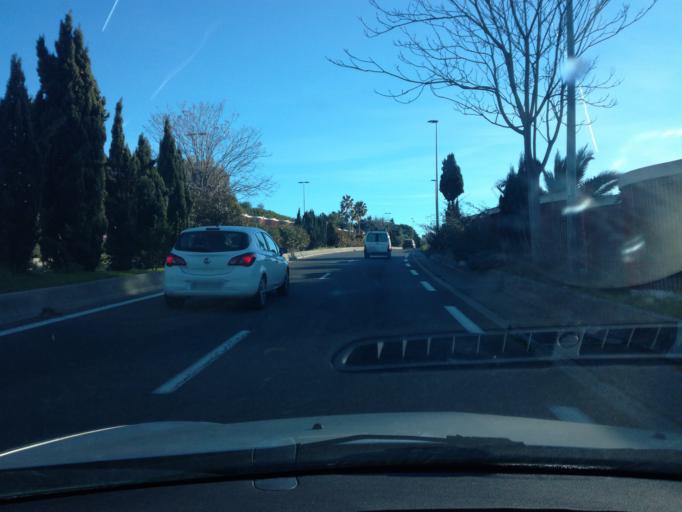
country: FR
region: Provence-Alpes-Cote d'Azur
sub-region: Departement des Alpes-Maritimes
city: Antibes
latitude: 43.5795
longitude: 7.0954
